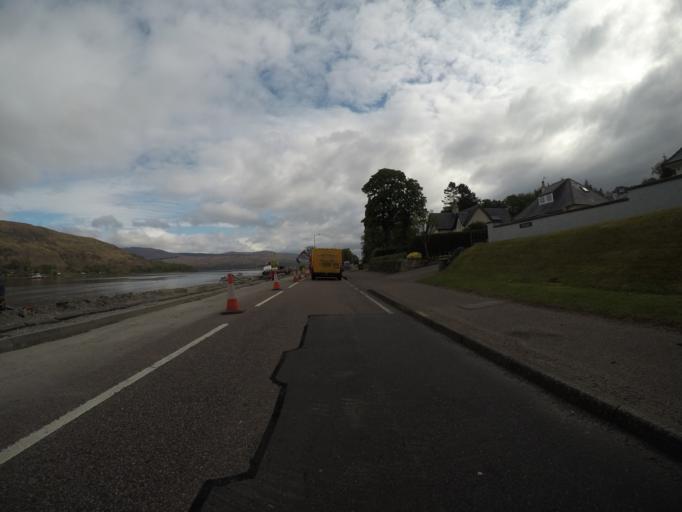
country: GB
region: Scotland
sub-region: Highland
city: Fort William
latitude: 56.8089
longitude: -5.1258
